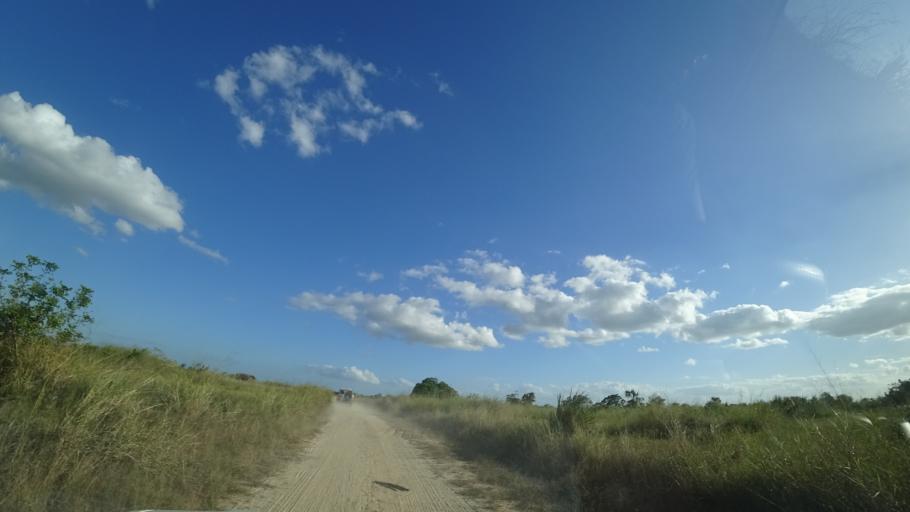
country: MZ
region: Sofala
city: Dondo
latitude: -19.4179
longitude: 34.5653
